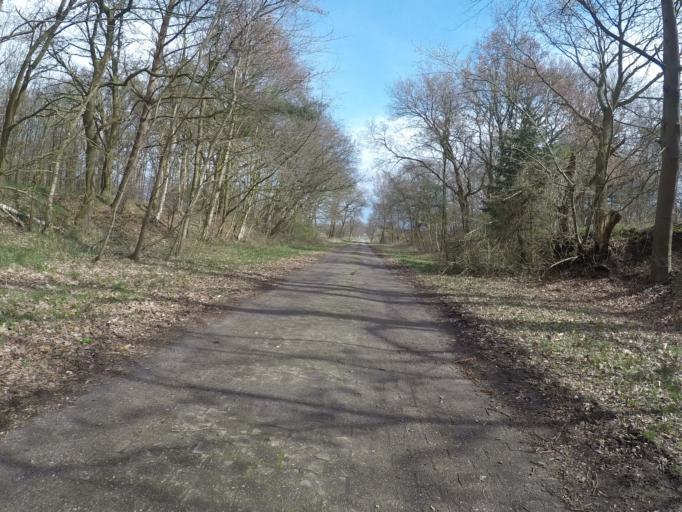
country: DE
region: Lower Saxony
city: Elmlohe
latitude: 53.6034
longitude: 8.6924
